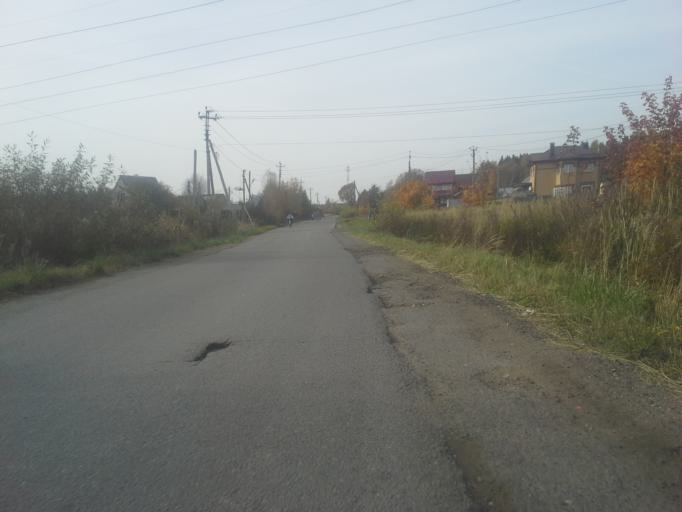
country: RU
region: Moskovskaya
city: Aprelevka
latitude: 55.5579
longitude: 37.0541
